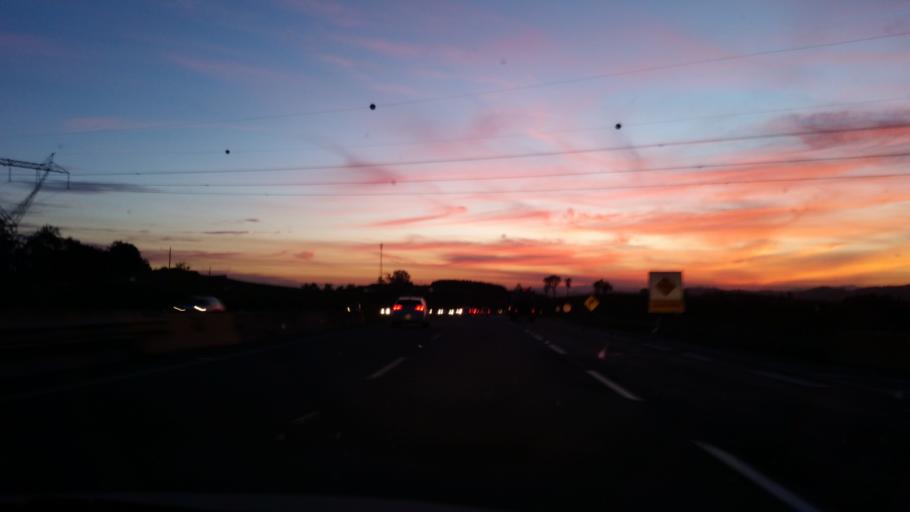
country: BR
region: Sao Paulo
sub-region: Guararema
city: Guararema
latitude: -23.3595
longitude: -46.1010
